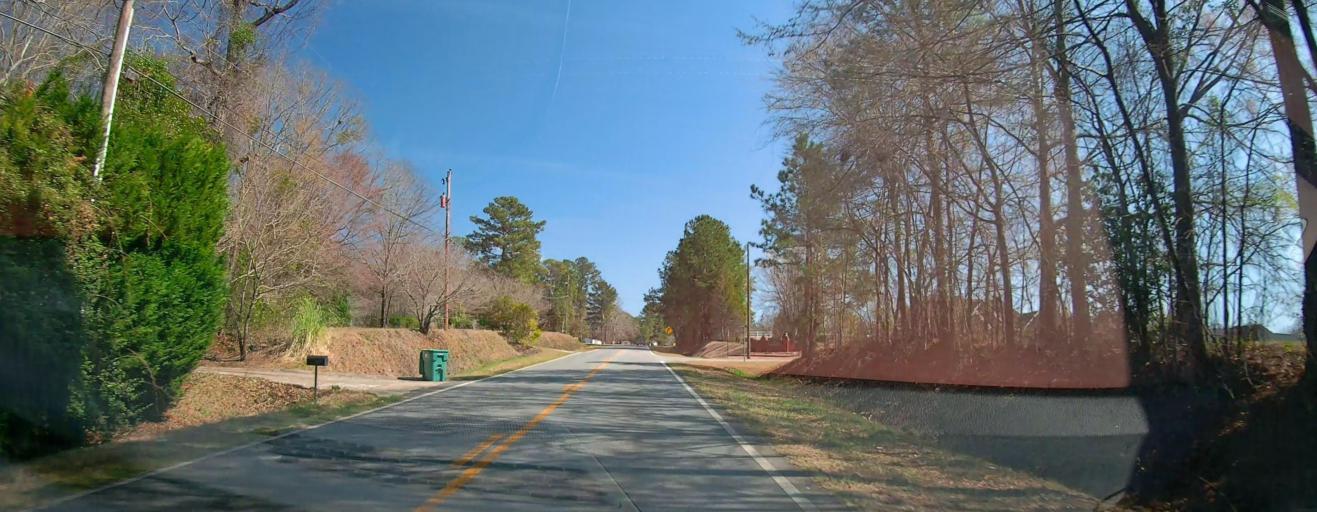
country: US
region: Georgia
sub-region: Bibb County
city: Macon
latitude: 32.8885
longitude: -83.5806
